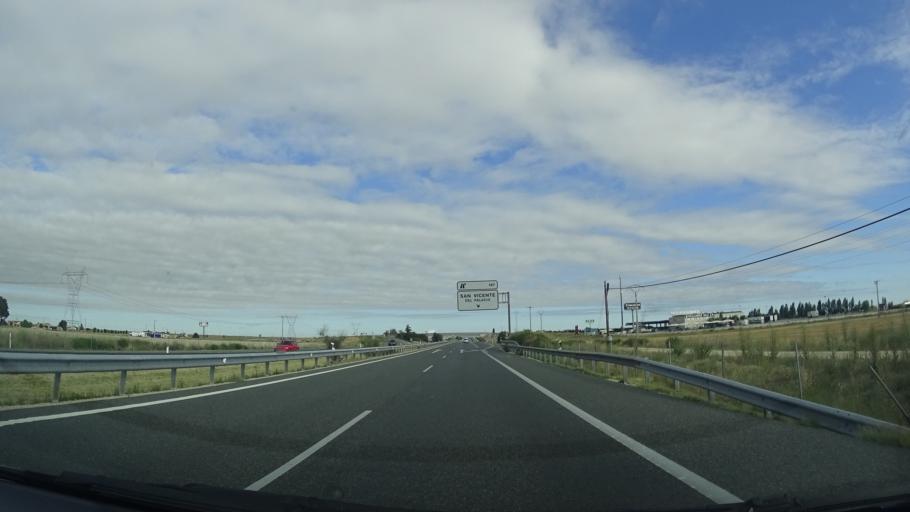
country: ES
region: Castille and Leon
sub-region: Provincia de Valladolid
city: San Vicente del Palacio
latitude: 41.2185
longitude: -4.8405
